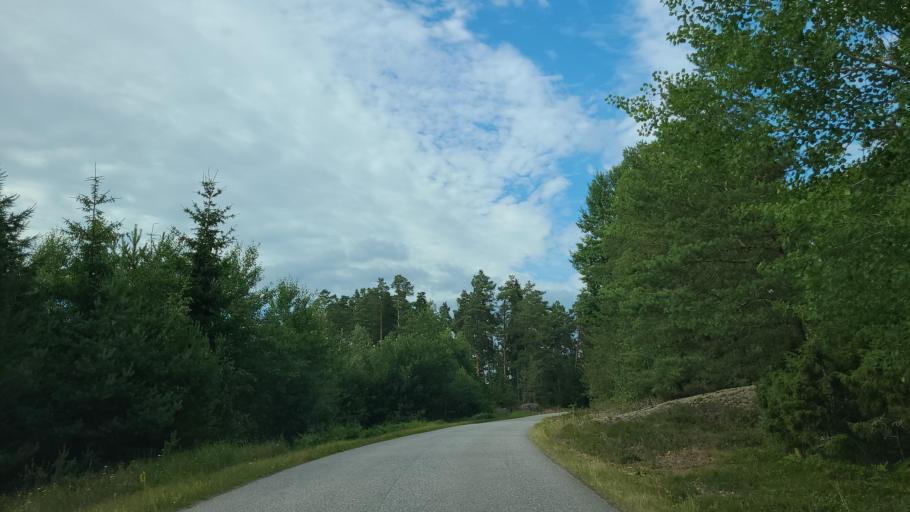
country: FI
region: Varsinais-Suomi
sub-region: Turku
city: Rymaettylae
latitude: 60.3070
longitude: 21.9403
